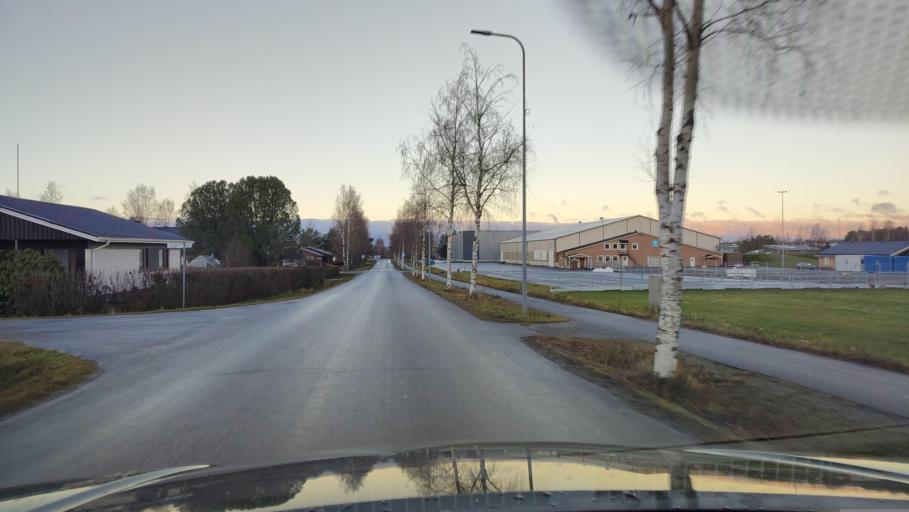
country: FI
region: Ostrobothnia
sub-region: Sydosterbotten
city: Naerpes
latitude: 62.4748
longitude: 21.3644
